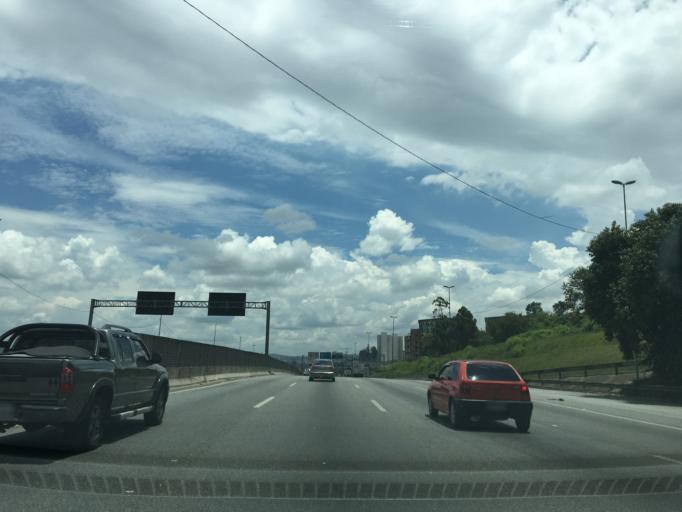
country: BR
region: Sao Paulo
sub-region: Guarulhos
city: Guarulhos
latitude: -23.4955
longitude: -46.5595
